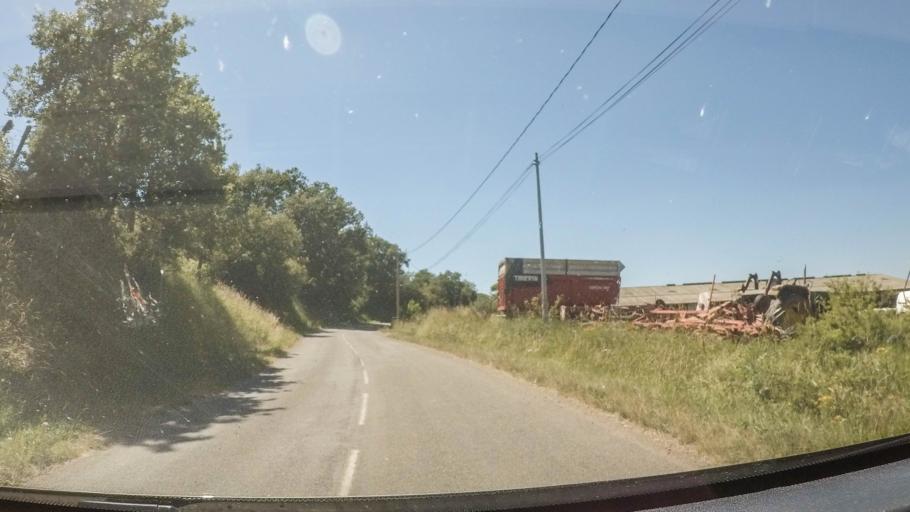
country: FR
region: Midi-Pyrenees
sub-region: Departement de l'Aveyron
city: Saint-Christophe-Vallon
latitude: 44.4715
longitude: 2.3636
